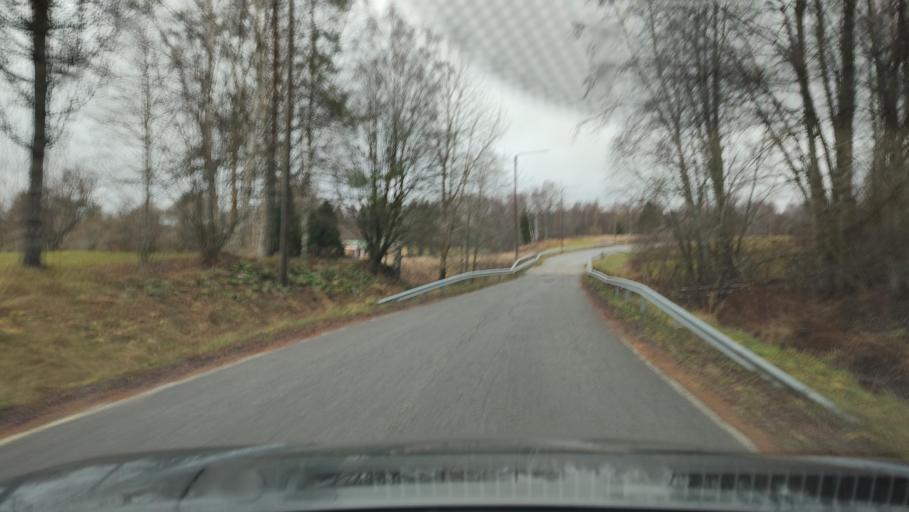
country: FI
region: Southern Ostrobothnia
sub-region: Suupohja
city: Isojoki
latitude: 62.1797
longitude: 21.9055
